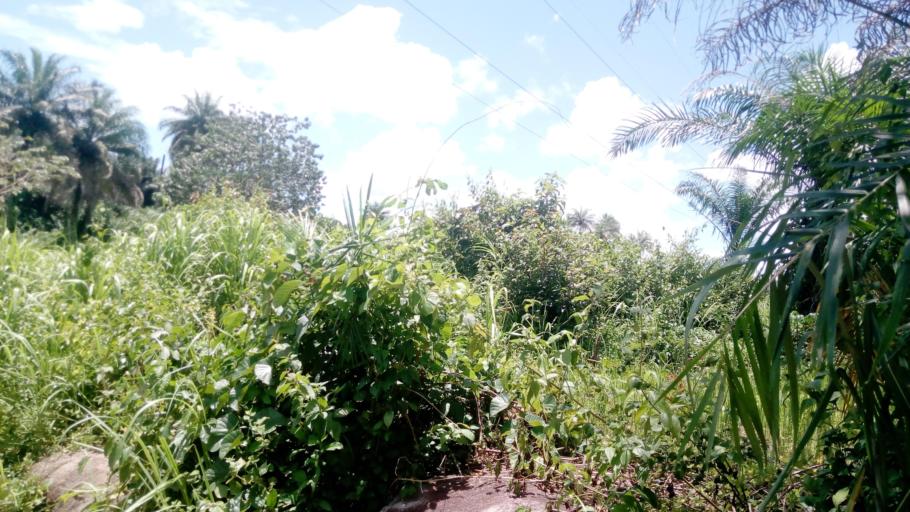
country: SL
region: Northern Province
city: Binkolo
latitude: 8.9206
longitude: -12.0080
